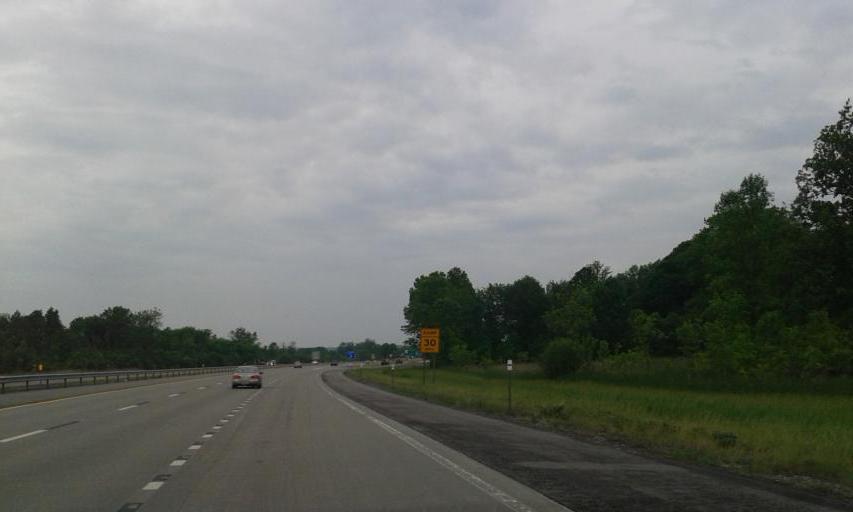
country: US
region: New York
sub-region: Onondaga County
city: Seneca Knolls
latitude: 43.0939
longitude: -76.3146
